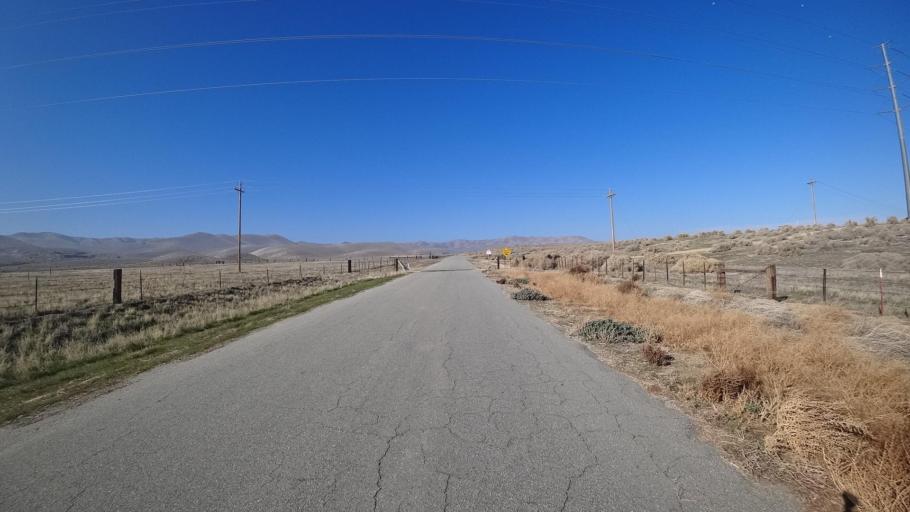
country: US
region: California
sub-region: Kern County
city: Taft Heights
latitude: 35.2273
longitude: -119.6336
